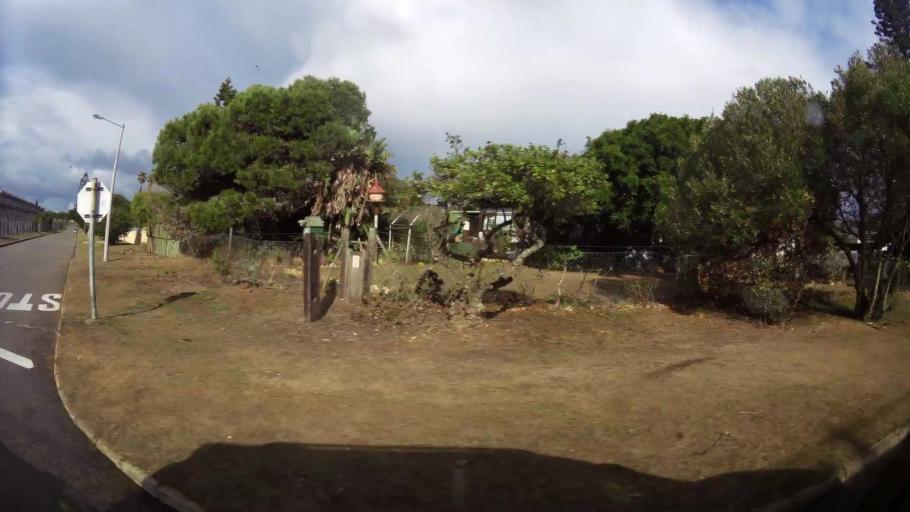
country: ZA
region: Western Cape
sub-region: Eden District Municipality
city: Mossel Bay
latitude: -34.1895
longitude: 22.1393
